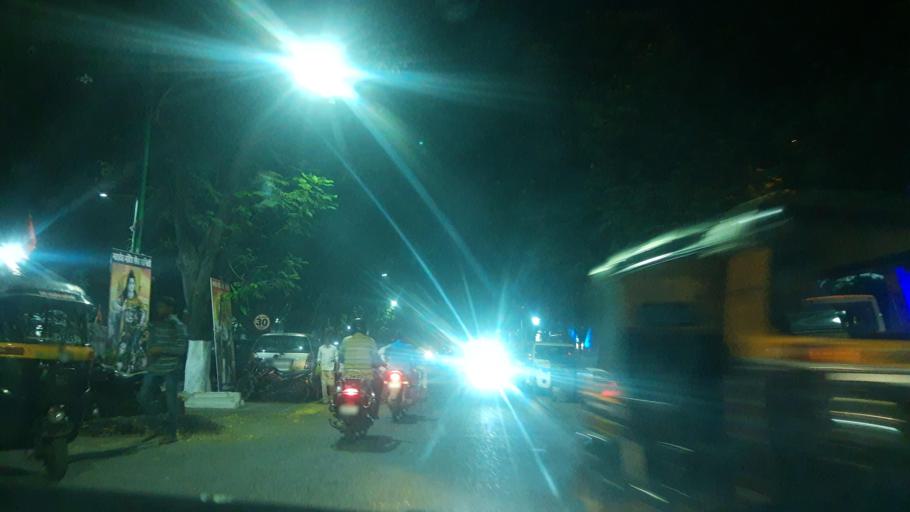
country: IN
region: Maharashtra
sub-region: Thane
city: Thane
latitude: 19.2006
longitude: 72.9652
